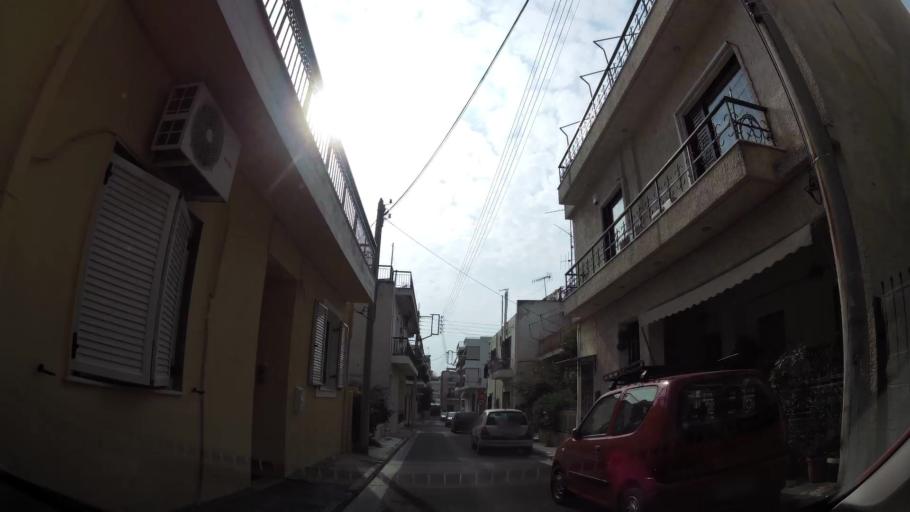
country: GR
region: Attica
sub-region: Nomarchia Athinas
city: Petroupolis
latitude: 38.0308
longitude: 23.6863
